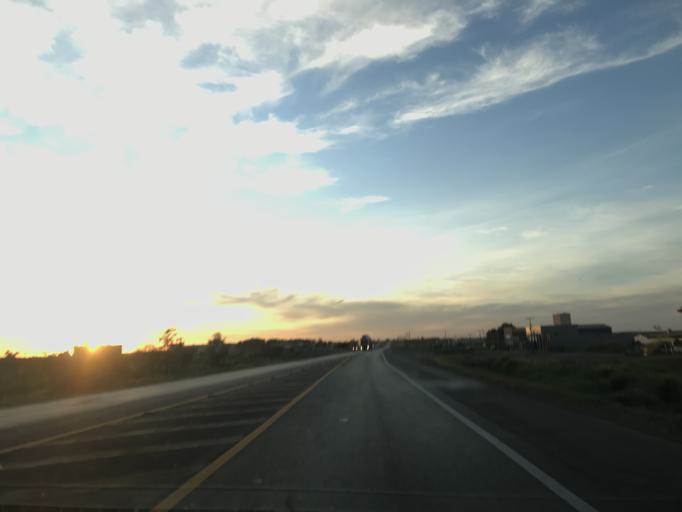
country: BR
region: Goias
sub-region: Luziania
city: Luziania
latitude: -16.2497
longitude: -47.9030
